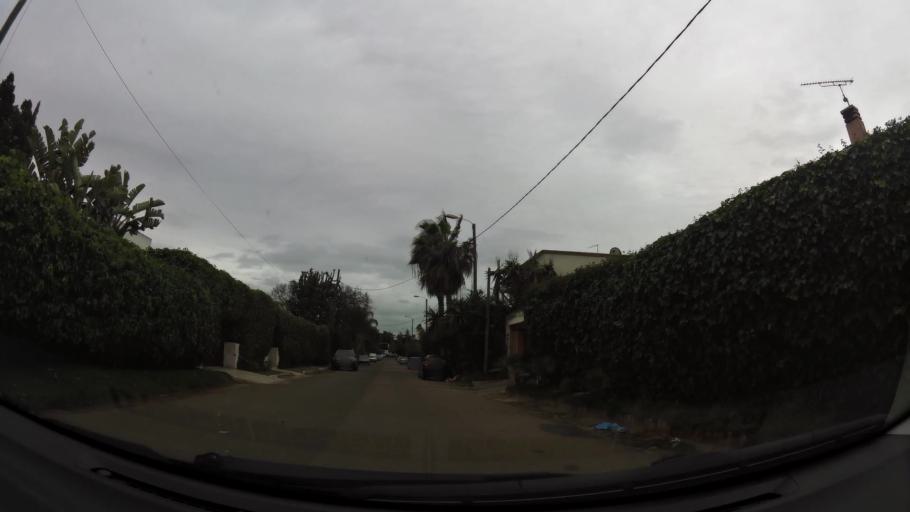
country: MA
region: Grand Casablanca
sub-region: Casablanca
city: Casablanca
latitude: 33.5806
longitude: -7.6559
